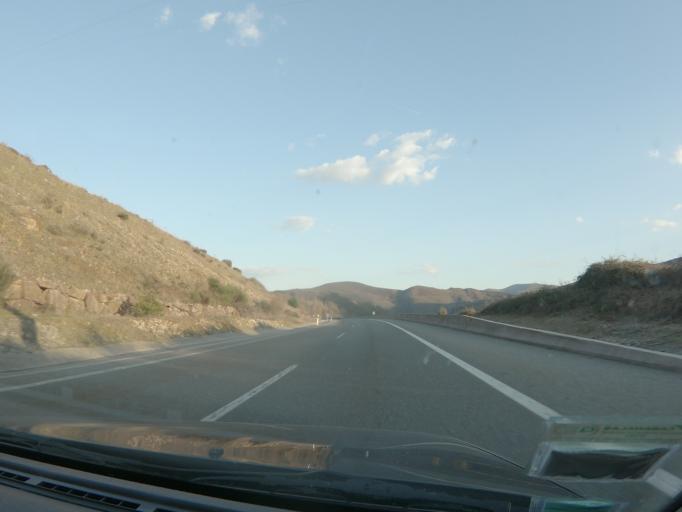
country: ES
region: Castille and Leon
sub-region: Provincia de Leon
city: Vega de Valcarce
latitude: 42.6727
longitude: -6.9594
